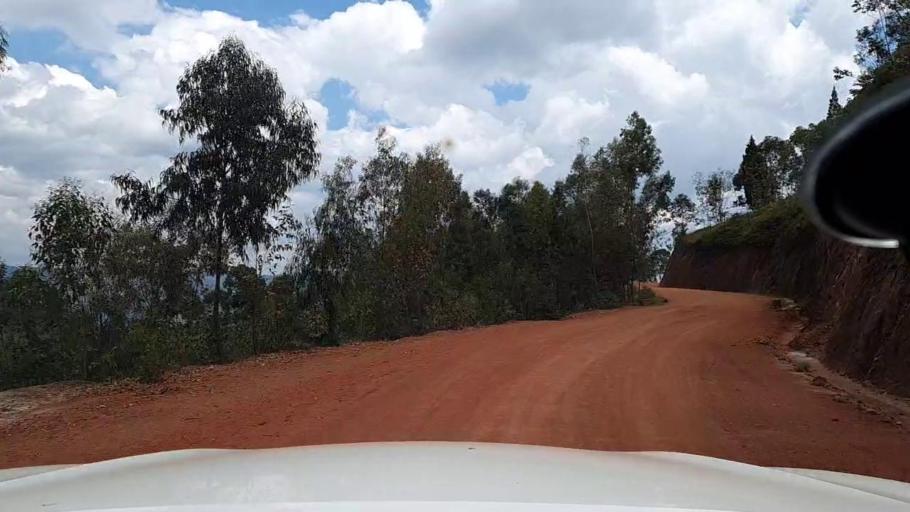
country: RW
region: Kigali
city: Kigali
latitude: -1.7847
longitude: 29.8443
